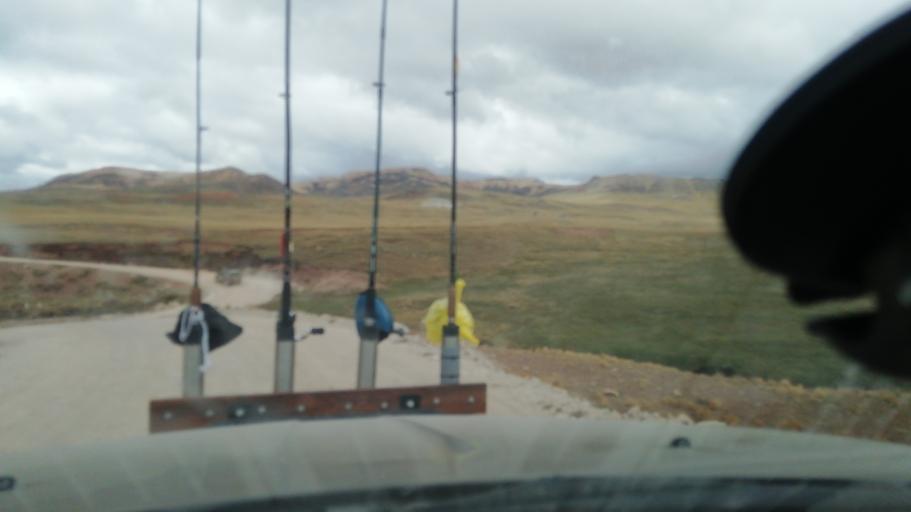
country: PE
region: Huancavelica
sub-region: Provincia de Huancavelica
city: Acobambilla
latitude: -12.5459
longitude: -75.5480
